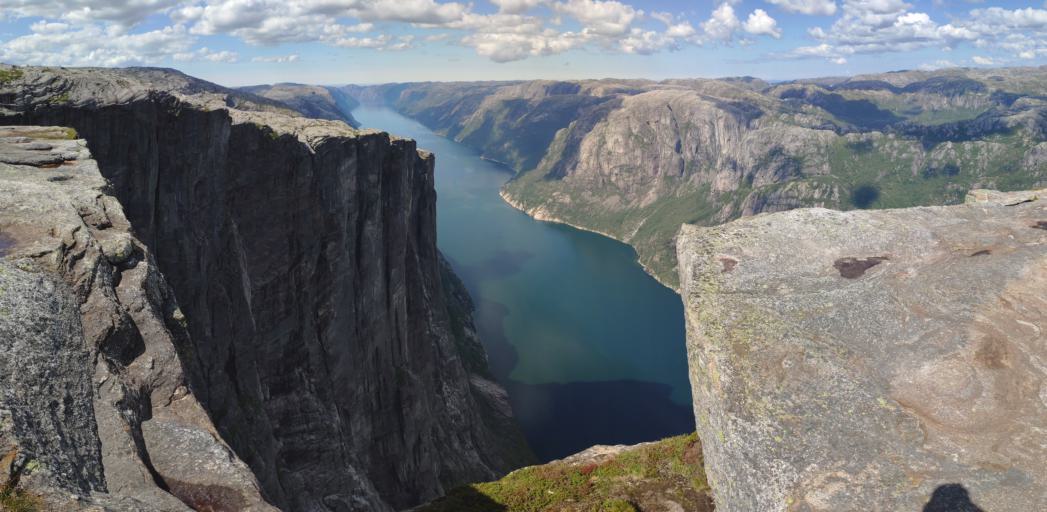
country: NO
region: Vest-Agder
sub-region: Sirdal
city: Tonstad
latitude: 59.0354
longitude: 6.5917
